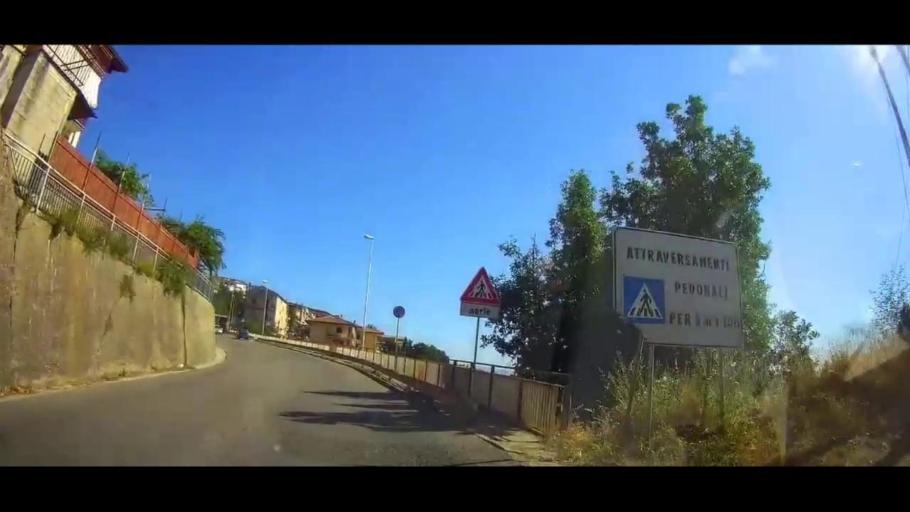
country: IT
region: Calabria
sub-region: Provincia di Cosenza
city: Celico
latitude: 39.3066
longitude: 16.3411
